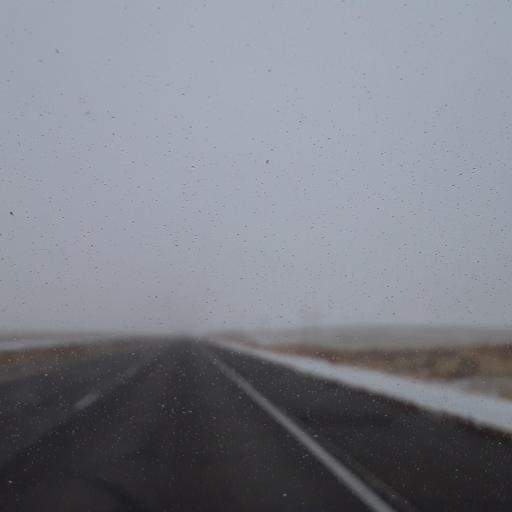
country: US
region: Nebraska
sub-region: Cheyenne County
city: Sidney
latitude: 40.7942
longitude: -102.8821
